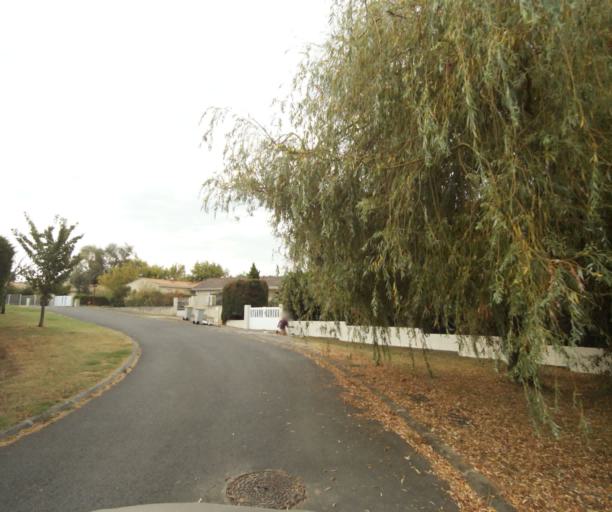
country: FR
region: Aquitaine
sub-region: Departement de la Gironde
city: Creon
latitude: 44.7676
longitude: -0.3460
